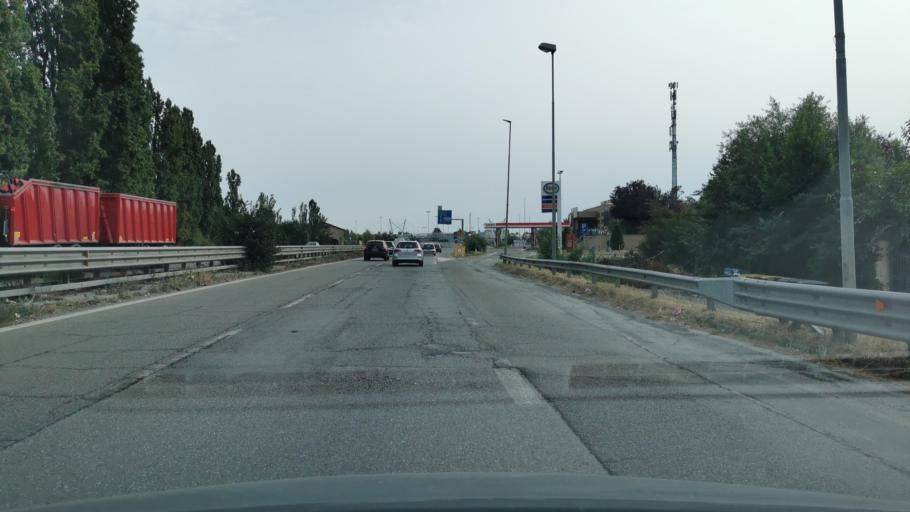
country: IT
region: Emilia-Romagna
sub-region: Provincia di Modena
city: Modena
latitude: 44.6295
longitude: 10.9536
